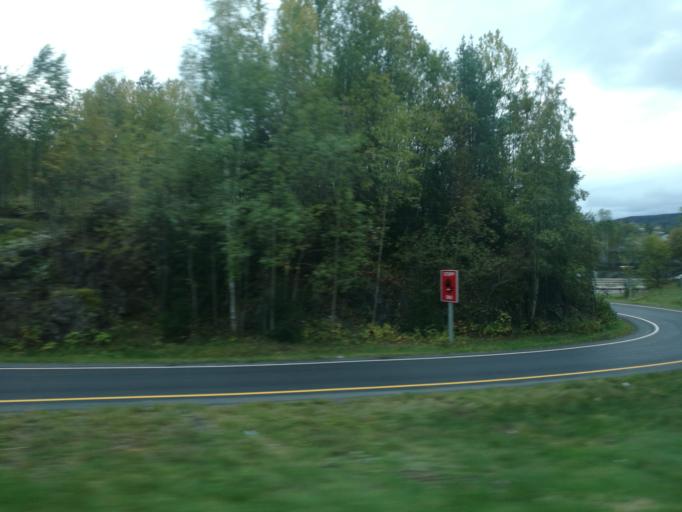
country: NO
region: Akershus
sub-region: Lorenskog
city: Kjenn
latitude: 59.9322
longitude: 10.9461
